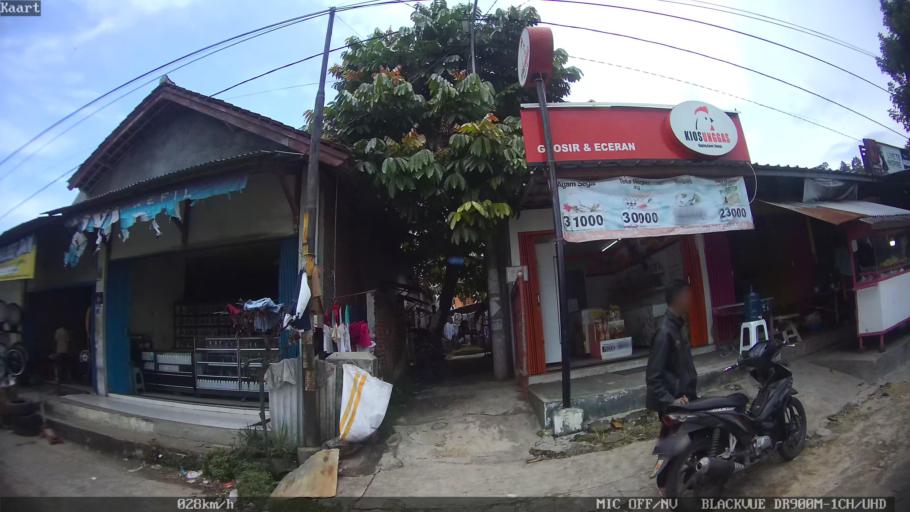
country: ID
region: Lampung
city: Bandarlampung
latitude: -5.4041
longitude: 105.2128
